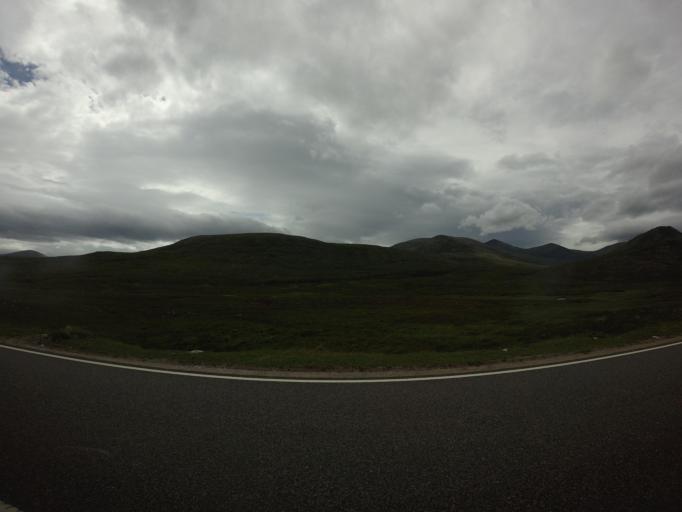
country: GB
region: Scotland
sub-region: Highland
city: Ullapool
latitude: 57.7370
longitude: -4.9525
